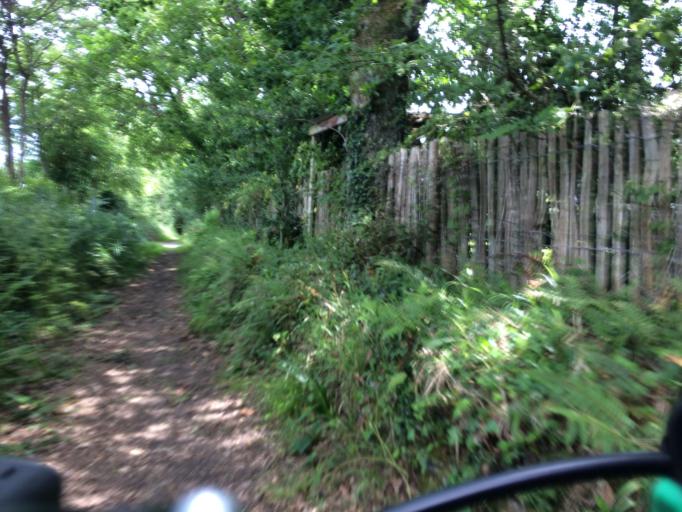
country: FR
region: Brittany
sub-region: Departement du Finistere
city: Logonna-Daoulas
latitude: 48.3172
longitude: -4.2927
